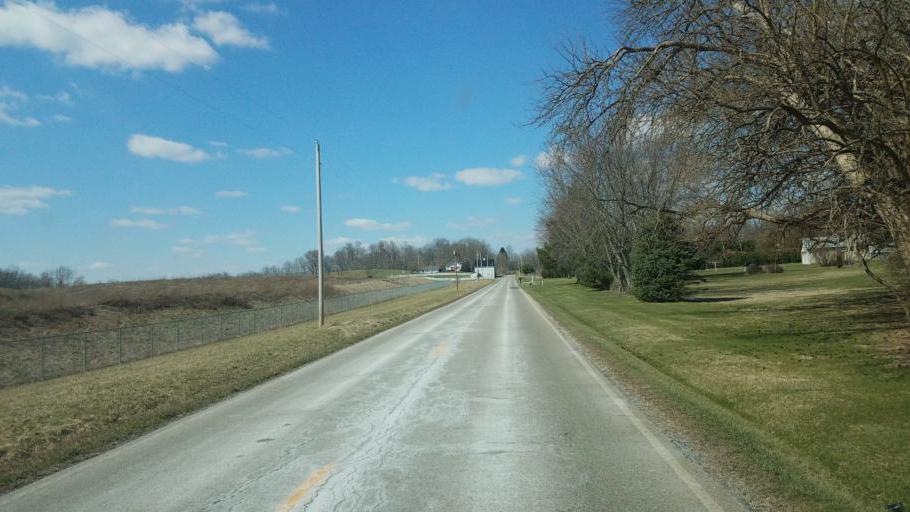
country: US
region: Ohio
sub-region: Knox County
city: Fredericktown
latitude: 40.4567
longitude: -82.5180
